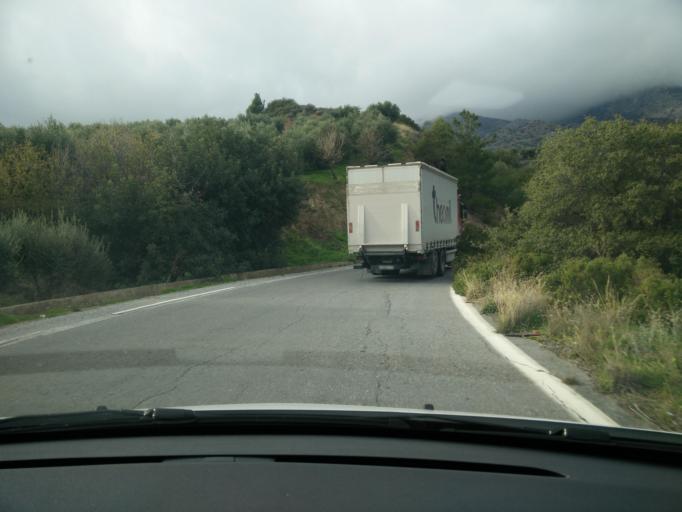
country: GR
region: Crete
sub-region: Nomos Lasithiou
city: Gra Liyia
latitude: 35.0227
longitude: 25.5703
